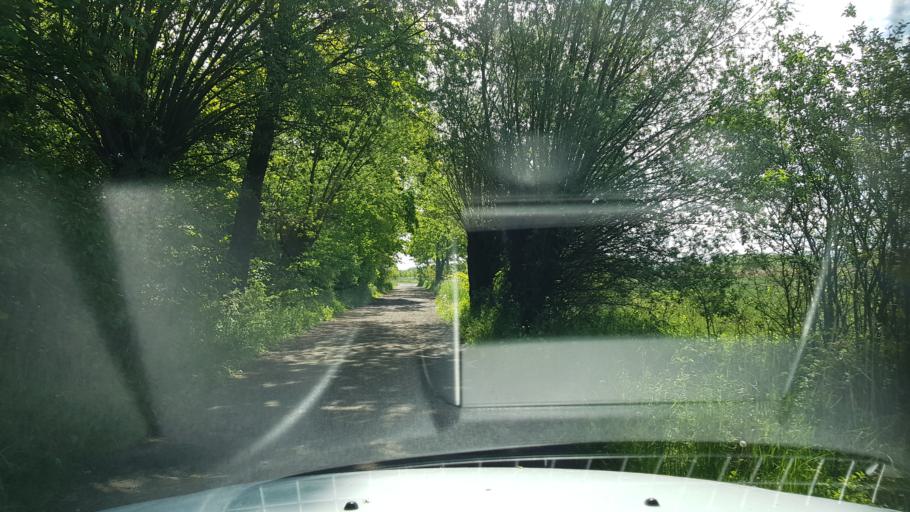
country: PL
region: West Pomeranian Voivodeship
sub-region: Powiat kolobrzeski
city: Ustronie Morskie
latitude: 54.2239
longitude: 15.8127
